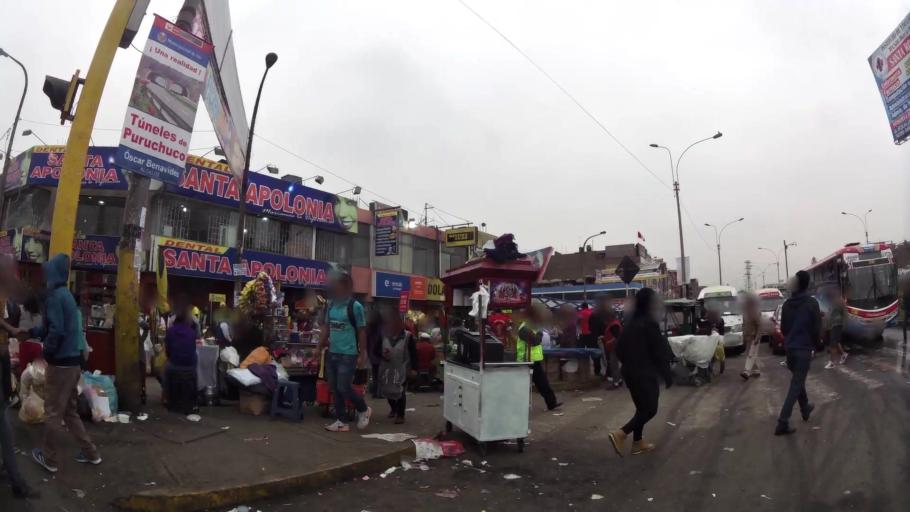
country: PE
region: Lima
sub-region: Lima
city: Vitarte
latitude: -12.0320
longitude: -76.9268
